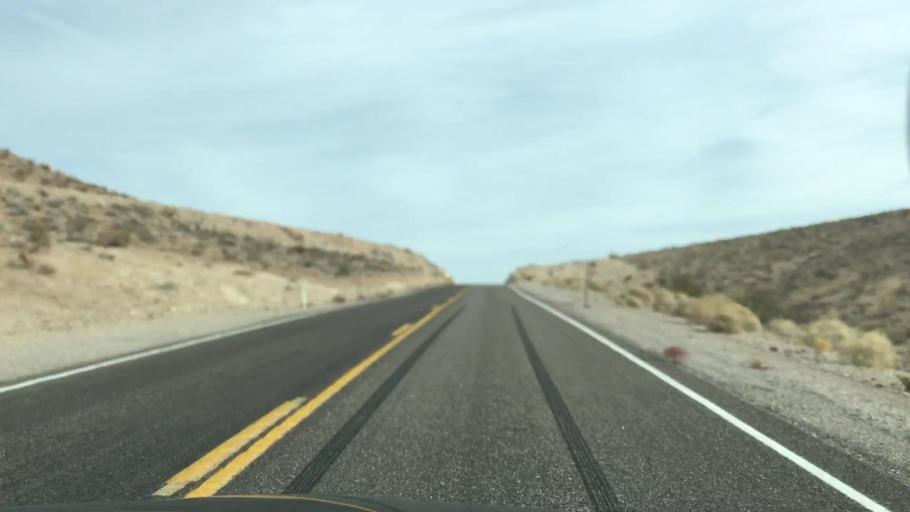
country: US
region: Nevada
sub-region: Nye County
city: Beatty
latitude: 36.8988
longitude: -116.7949
